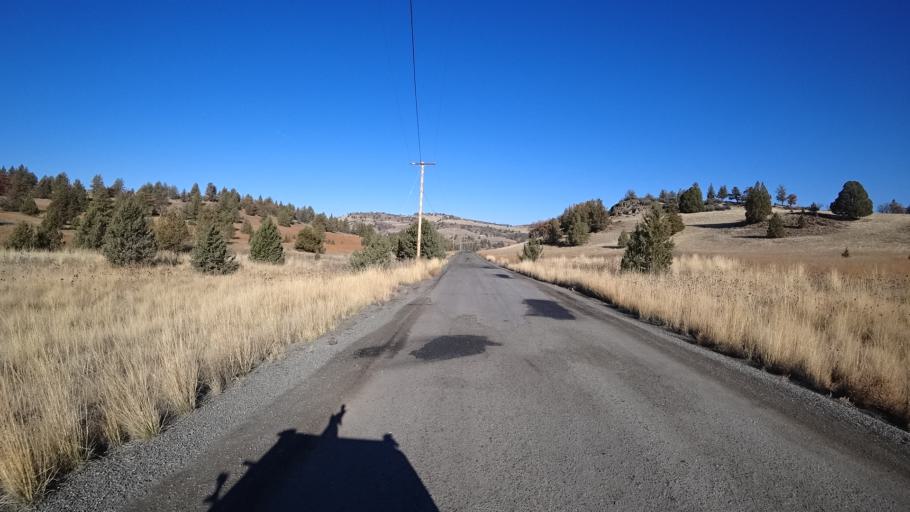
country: US
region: California
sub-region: Siskiyou County
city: Montague
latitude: 41.8842
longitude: -122.4260
